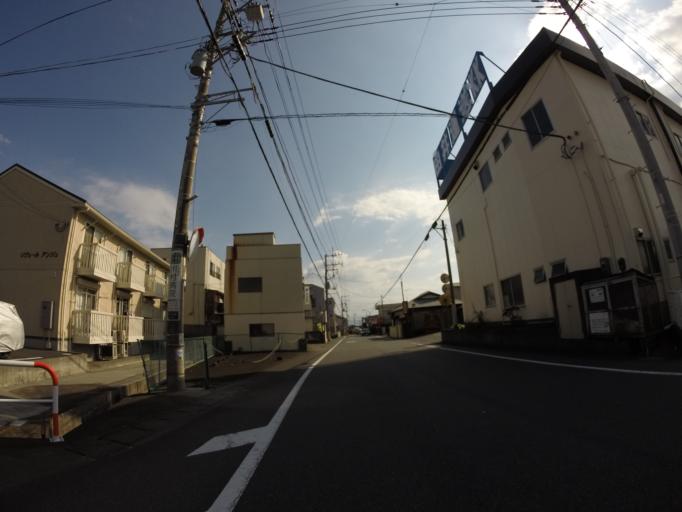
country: JP
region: Shizuoka
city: Fujinomiya
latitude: 35.1896
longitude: 138.6452
